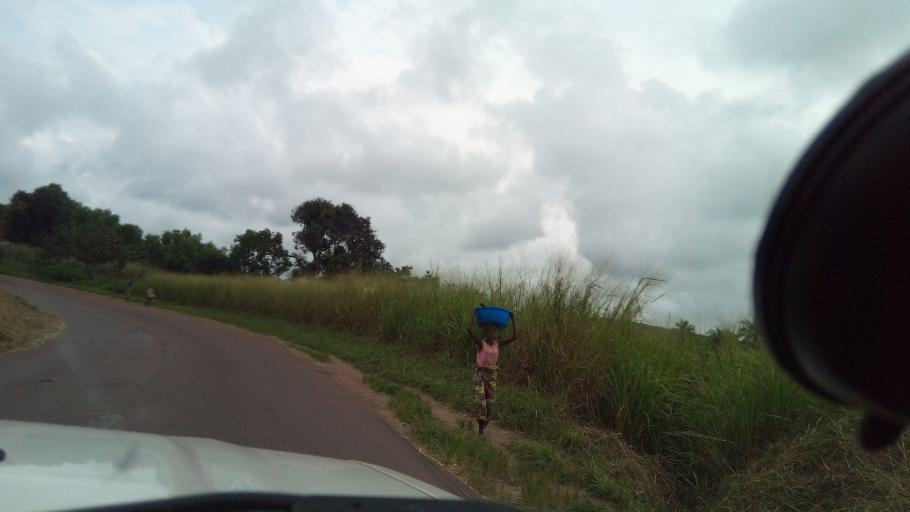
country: CD
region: Bas-Congo
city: Kasangulu
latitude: -4.8951
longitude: 15.1741
